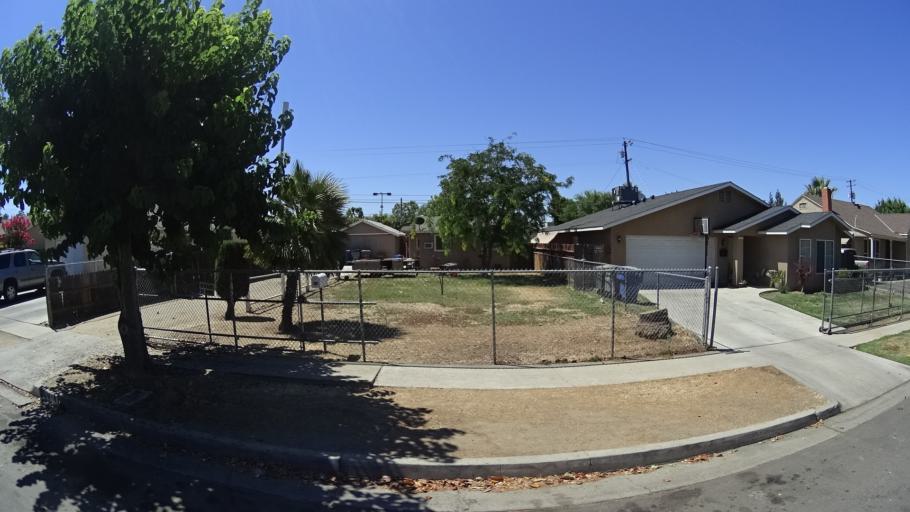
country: US
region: California
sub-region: Fresno County
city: Fresno
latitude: 36.7803
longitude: -119.8071
